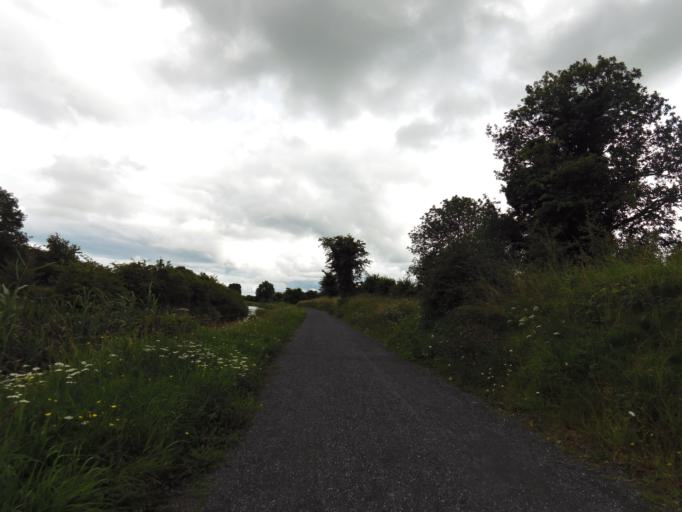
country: IE
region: Leinster
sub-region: An Iarmhi
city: An Muileann gCearr
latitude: 53.5298
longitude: -7.4595
